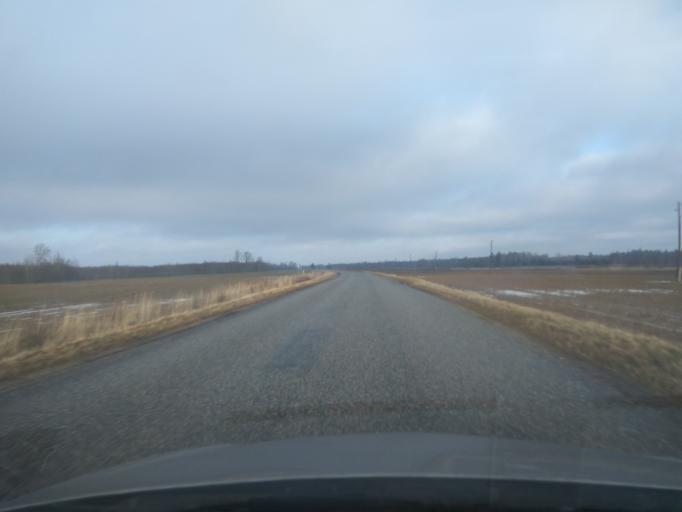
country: LV
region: Saldus Rajons
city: Saldus
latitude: 56.7672
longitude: 22.3867
